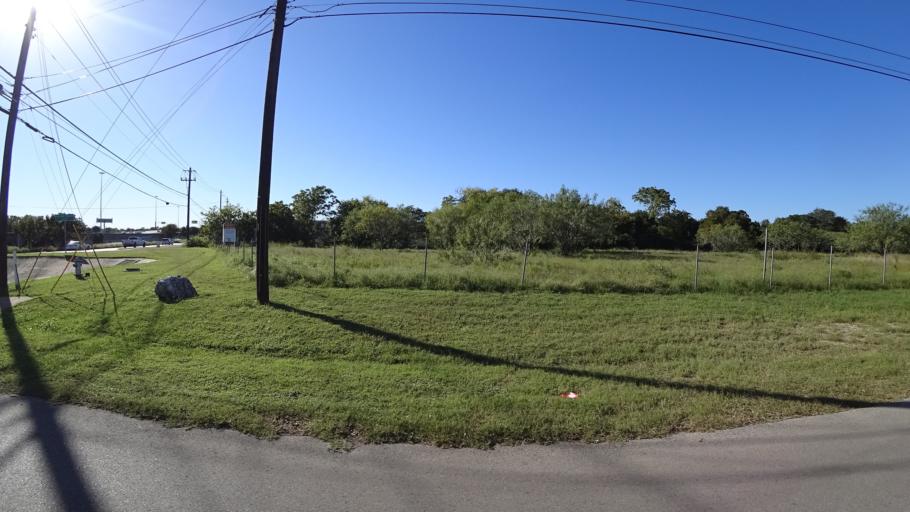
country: US
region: Texas
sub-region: Travis County
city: Rollingwood
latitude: 30.2342
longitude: -97.8110
